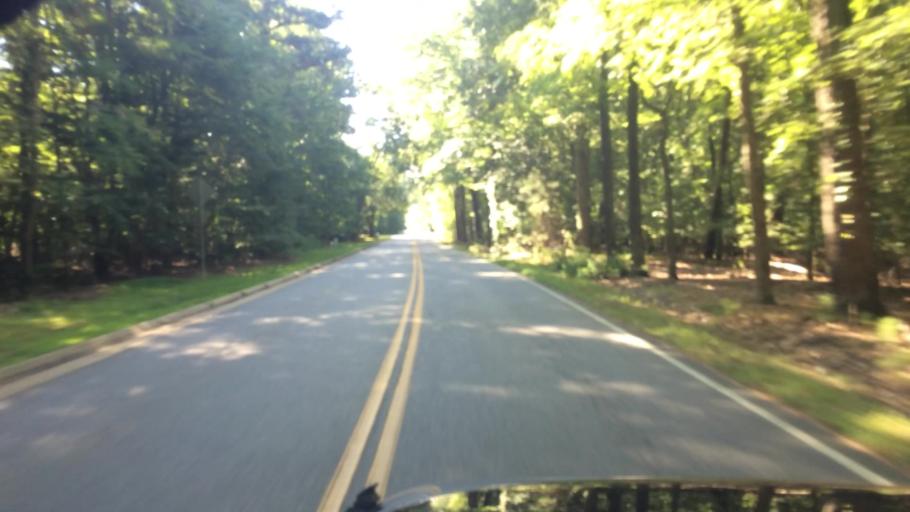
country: US
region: Virginia
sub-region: James City County
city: Williamsburg
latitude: 37.2408
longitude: -76.7900
